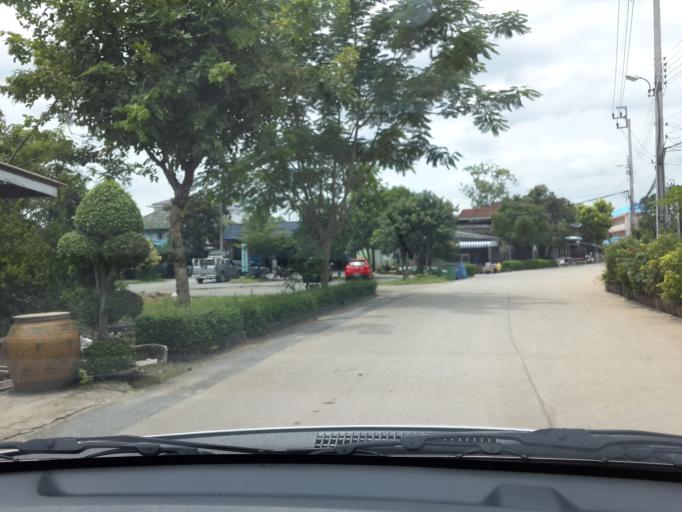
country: TH
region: Bangkok
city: Khlong Sam Wa
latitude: 13.8368
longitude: 100.7706
